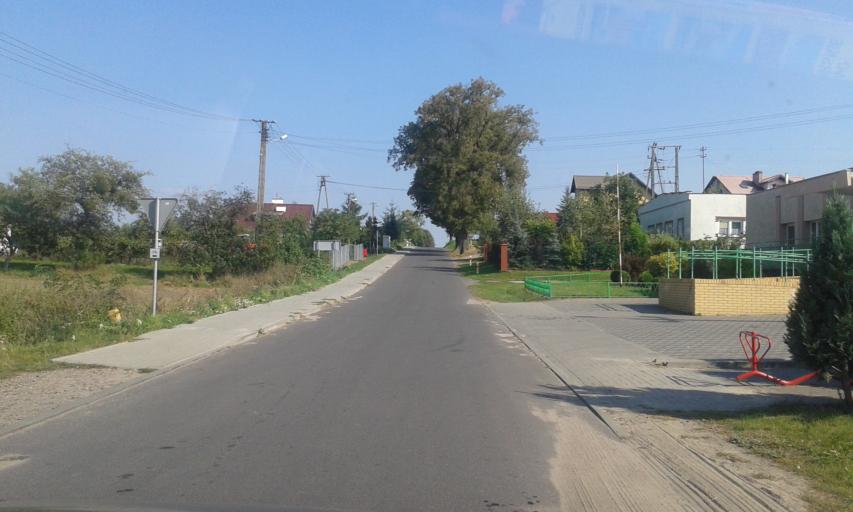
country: PL
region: Kujawsko-Pomorskie
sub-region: Powiat swiecki
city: Nowe
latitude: 53.6741
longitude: 18.7257
